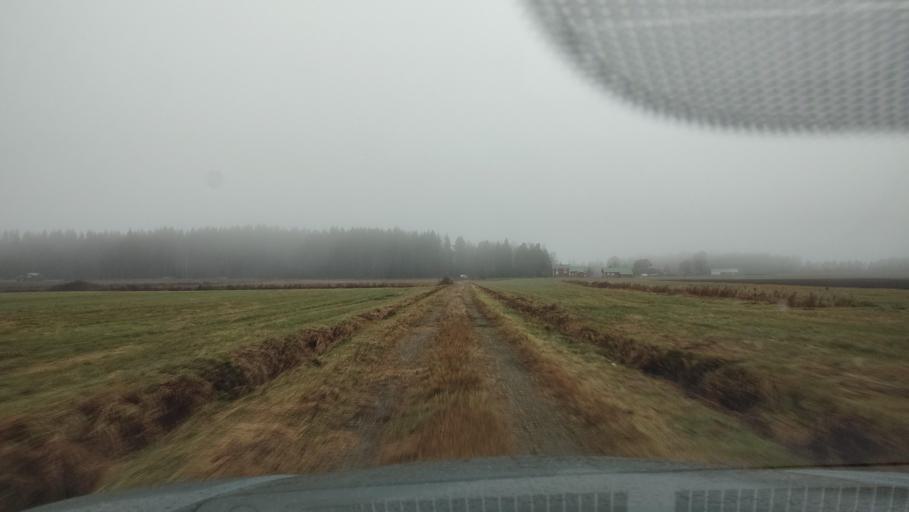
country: FI
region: Southern Ostrobothnia
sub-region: Suupohja
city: Karijoki
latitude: 62.1878
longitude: 21.7831
